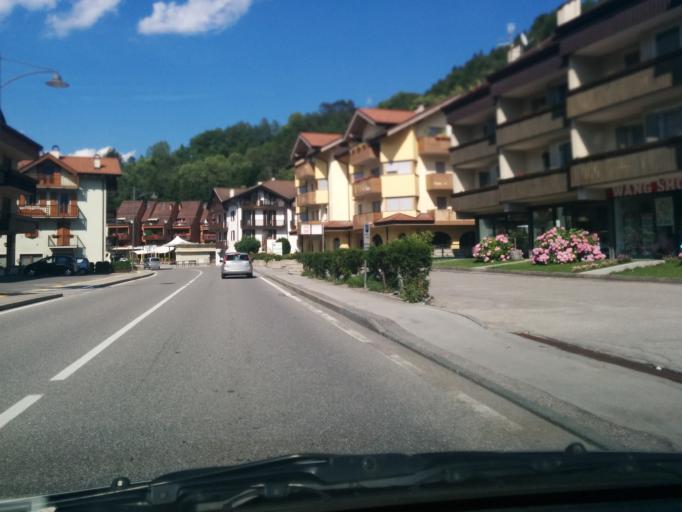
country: IT
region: Trentino-Alto Adige
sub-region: Provincia di Trento
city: Ponte Arche
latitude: 46.0359
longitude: 10.8741
